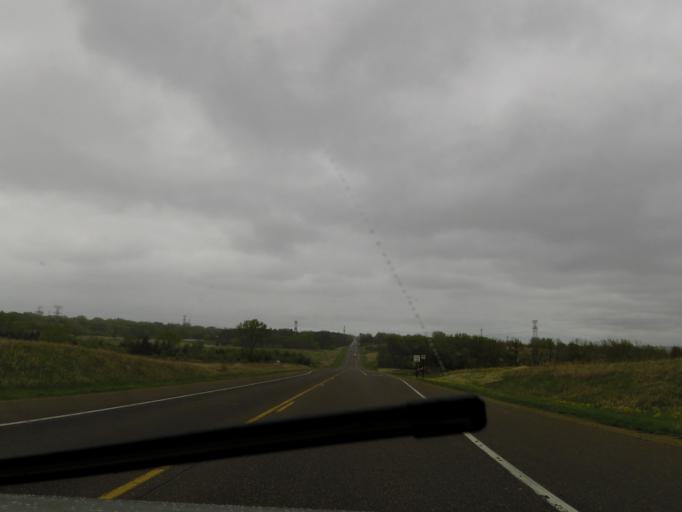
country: US
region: Minnesota
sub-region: Washington County
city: Oak Park Heights
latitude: 45.0224
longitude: -92.8073
